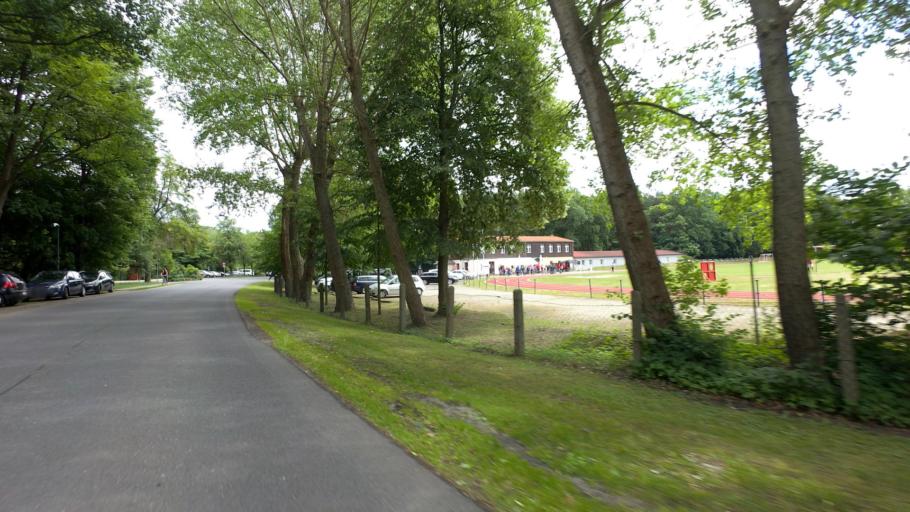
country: DE
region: Brandenburg
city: Luckau
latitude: 51.8531
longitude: 13.6936
